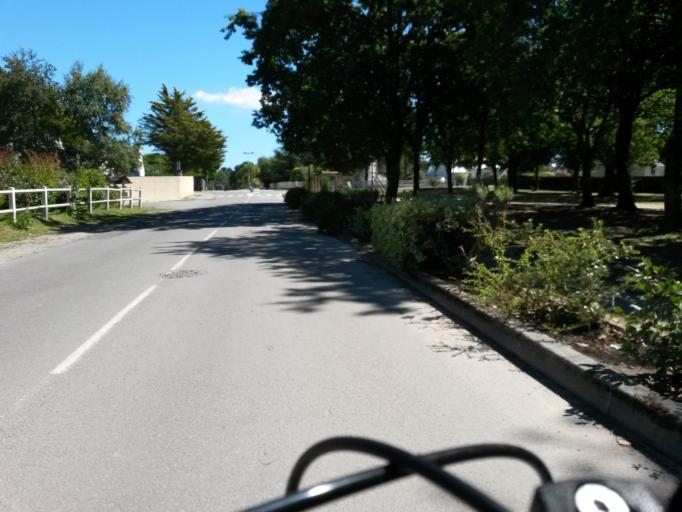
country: FR
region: Pays de la Loire
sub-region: Departement de la Loire-Atlantique
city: Mesquer
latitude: 47.4052
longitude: -2.4867
